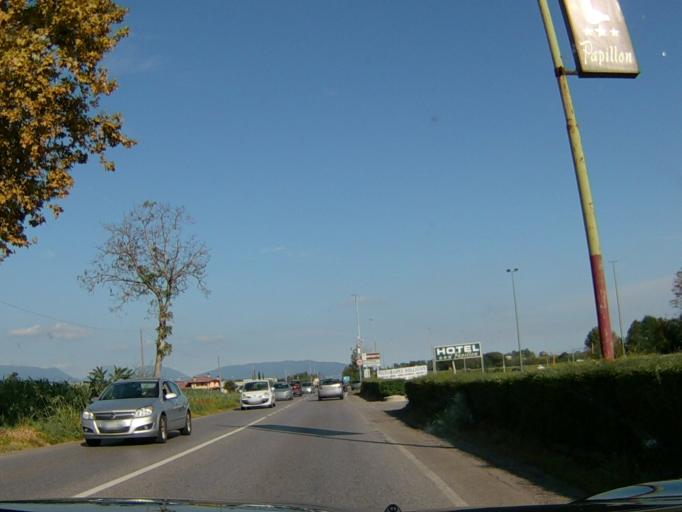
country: IT
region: Lombardy
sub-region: Provincia di Brescia
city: Lodetto
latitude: 45.5572
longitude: 10.0522
